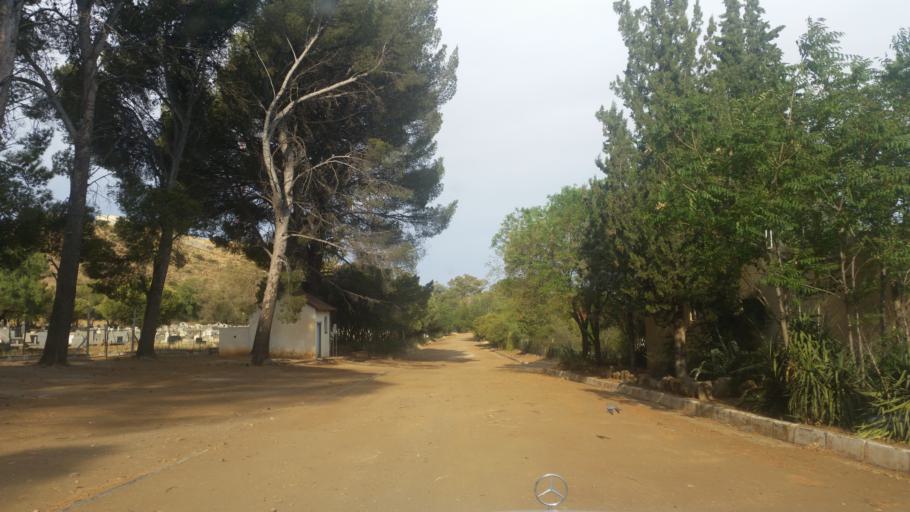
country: ZA
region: Orange Free State
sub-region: Xhariep District Municipality
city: Trompsburg
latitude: -30.4926
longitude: 25.9702
